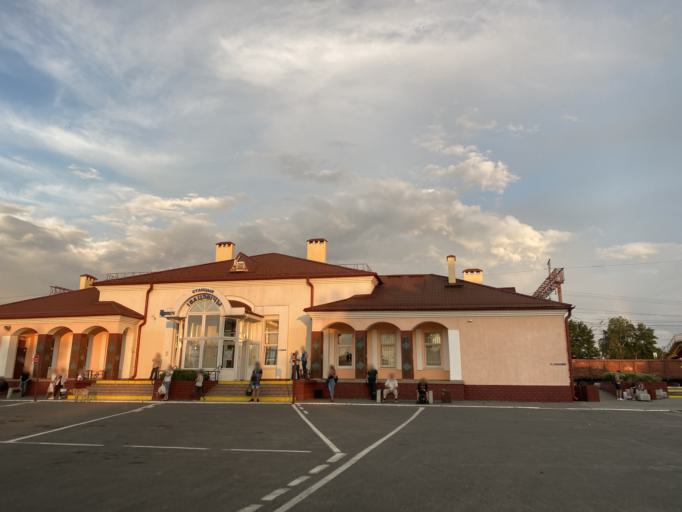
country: BY
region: Brest
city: Ivatsevichy
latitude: 52.7095
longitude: 25.3442
